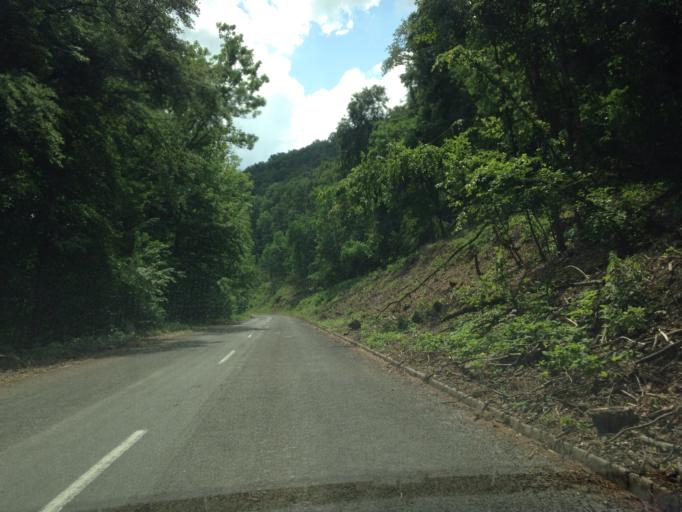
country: HU
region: Pest
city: Visegrad
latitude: 47.7506
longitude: 18.9425
